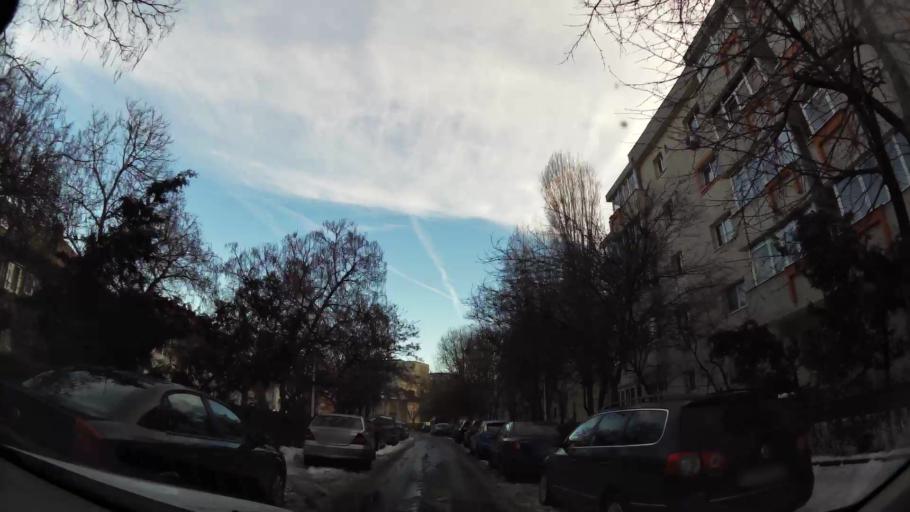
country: RO
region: Bucuresti
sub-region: Municipiul Bucuresti
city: Bucharest
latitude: 44.4243
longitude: 26.1321
